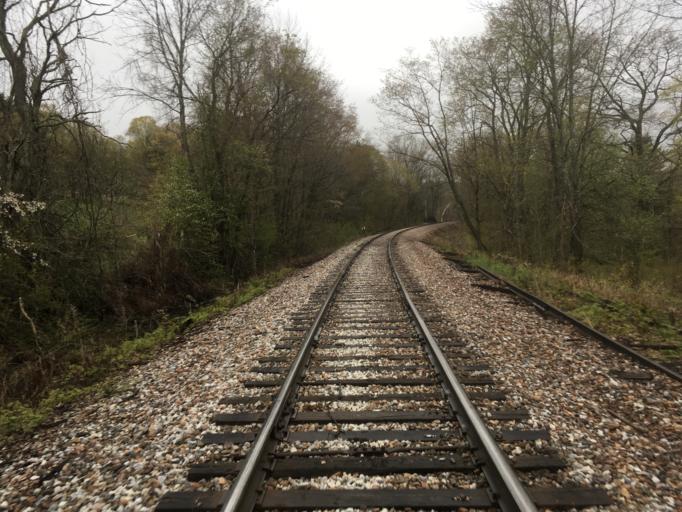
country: US
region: Vermont
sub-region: Rutland County
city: Rutland
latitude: 43.4898
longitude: -72.8782
